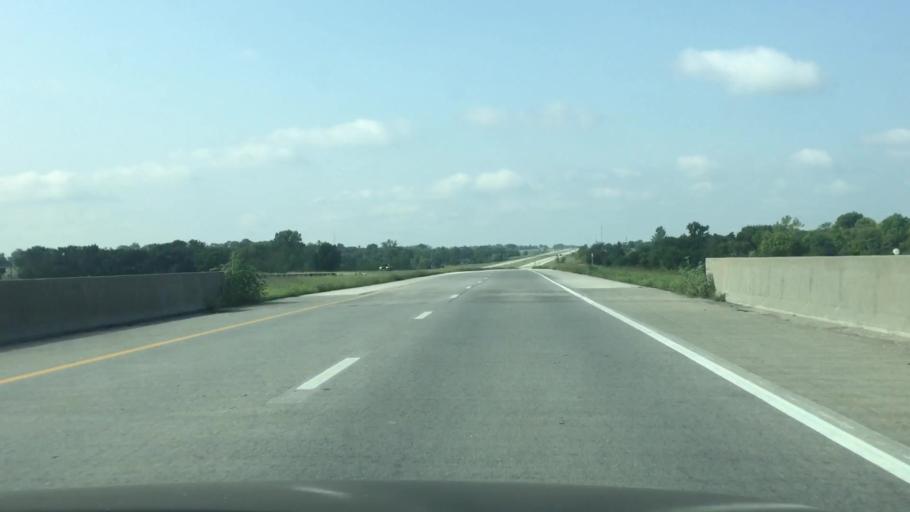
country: US
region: Kansas
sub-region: Miami County
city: Paola
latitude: 38.5517
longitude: -94.8734
